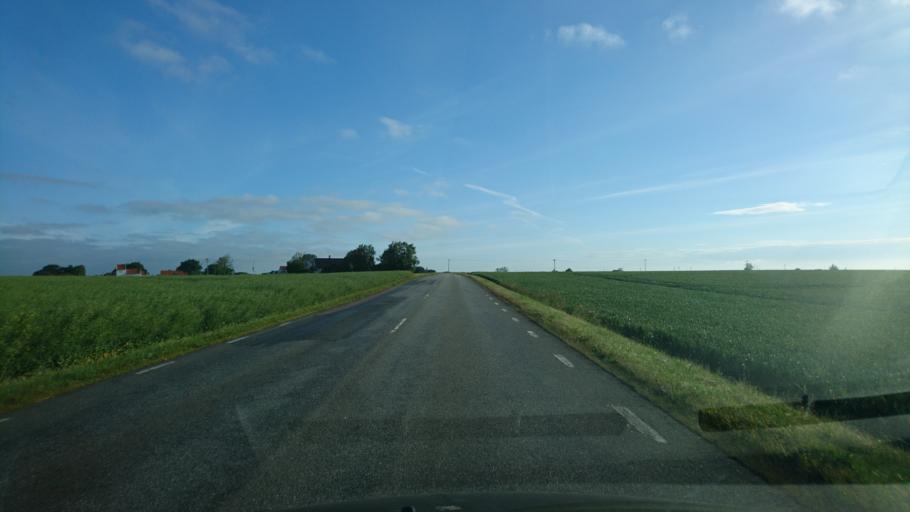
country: SE
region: Skane
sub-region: Tomelilla Kommun
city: Tomelilla
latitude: 55.4850
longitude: 14.1018
